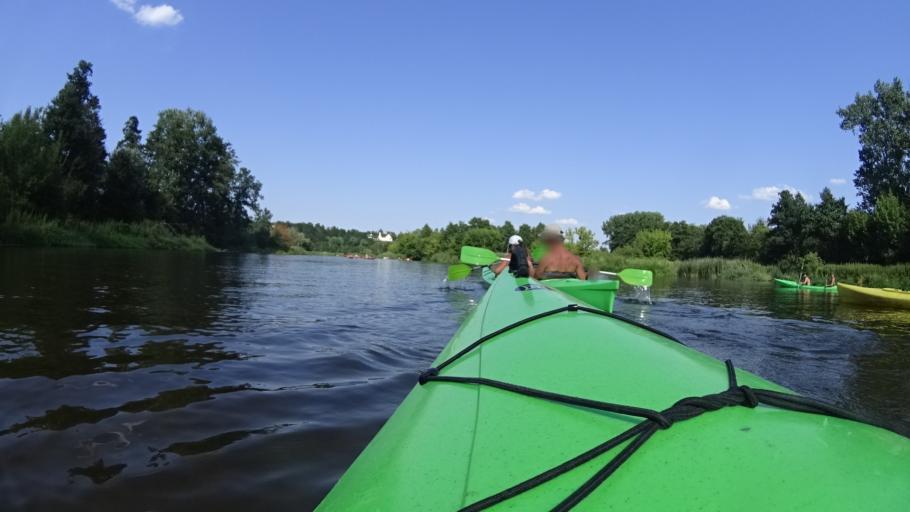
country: PL
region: Masovian Voivodeship
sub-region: Powiat bialobrzeski
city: Bialobrzegi
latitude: 51.6633
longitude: 20.9071
